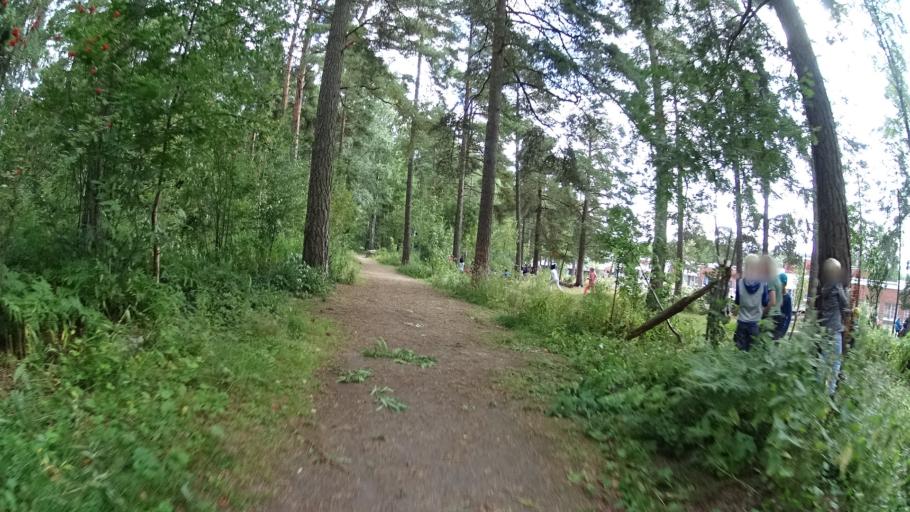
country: FI
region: Uusimaa
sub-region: Helsinki
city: Kilo
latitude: 60.2107
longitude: 24.7702
